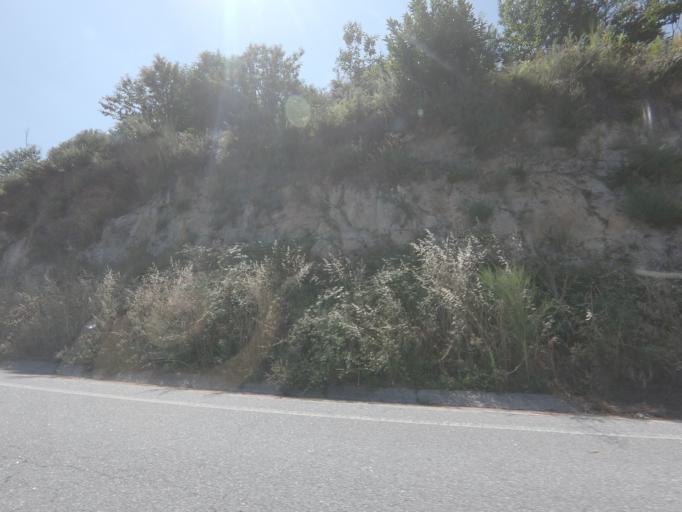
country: PT
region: Viseu
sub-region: Tarouca
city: Tarouca
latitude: 41.0125
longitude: -7.7840
